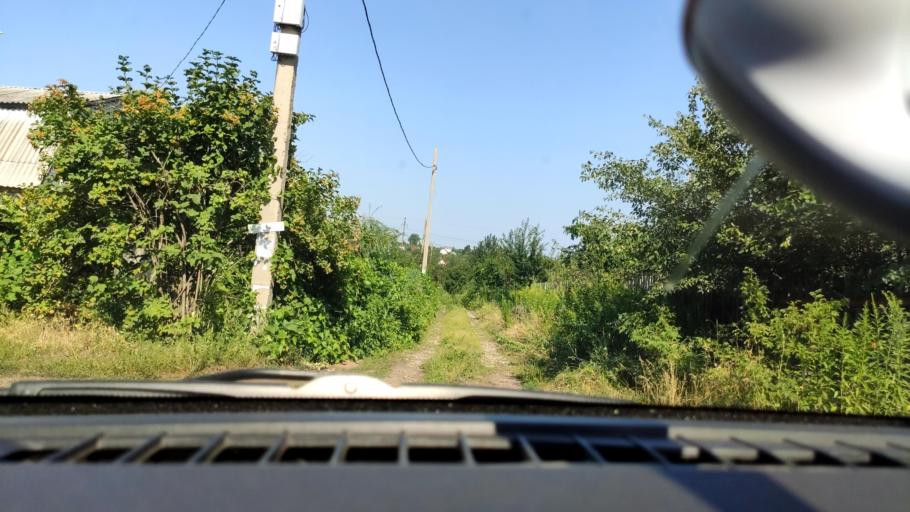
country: RU
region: Samara
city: Petra-Dubrava
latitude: 53.2699
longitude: 50.2989
